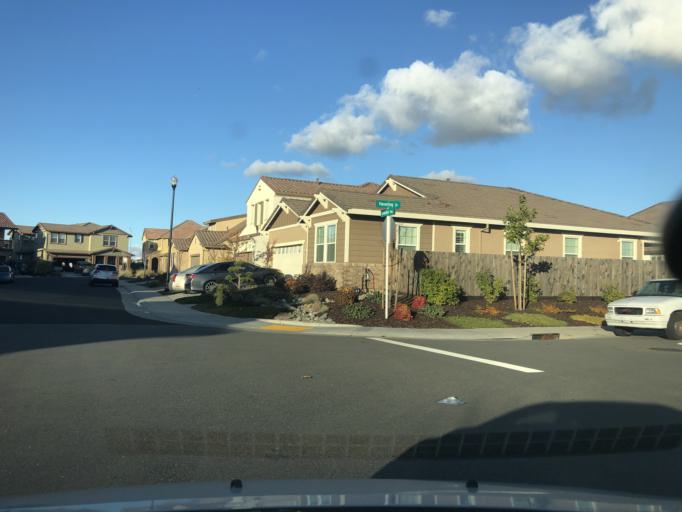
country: US
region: California
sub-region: Sacramento County
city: Antelope
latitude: 38.7740
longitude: -121.3844
